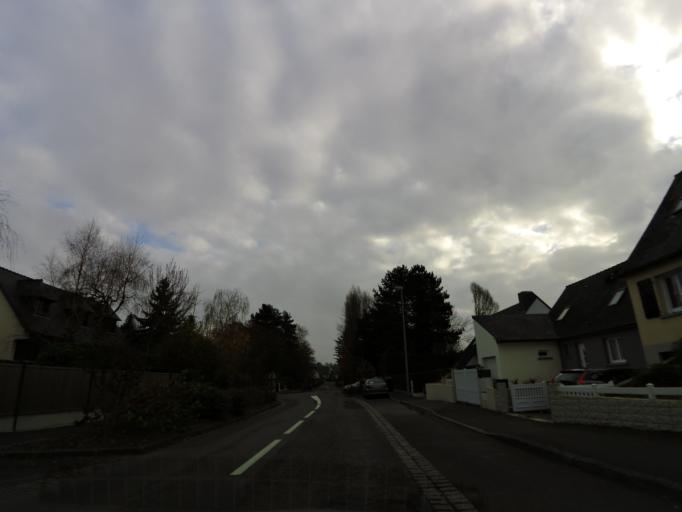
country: FR
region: Brittany
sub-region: Departement d'Ille-et-Vilaine
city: Orgeres
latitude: 47.9928
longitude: -1.6709
